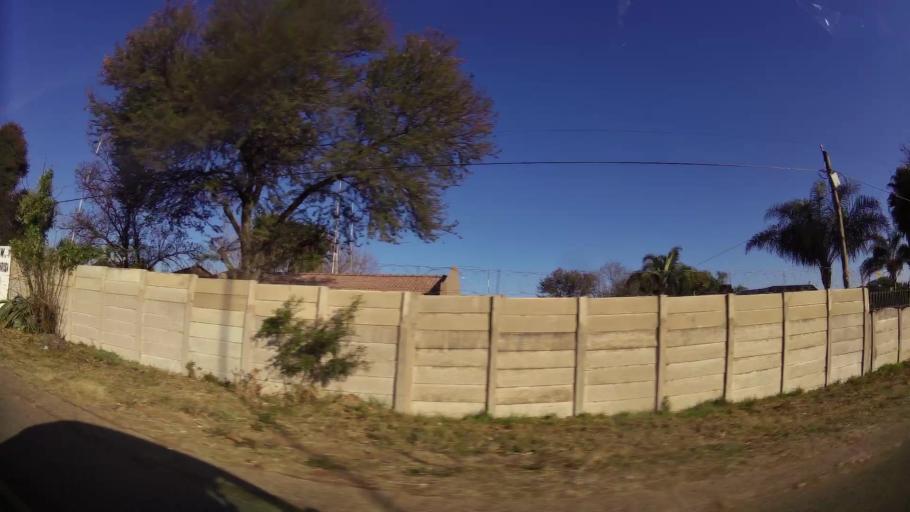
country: ZA
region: Gauteng
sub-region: City of Tshwane Metropolitan Municipality
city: Centurion
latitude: -25.8688
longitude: 28.1472
